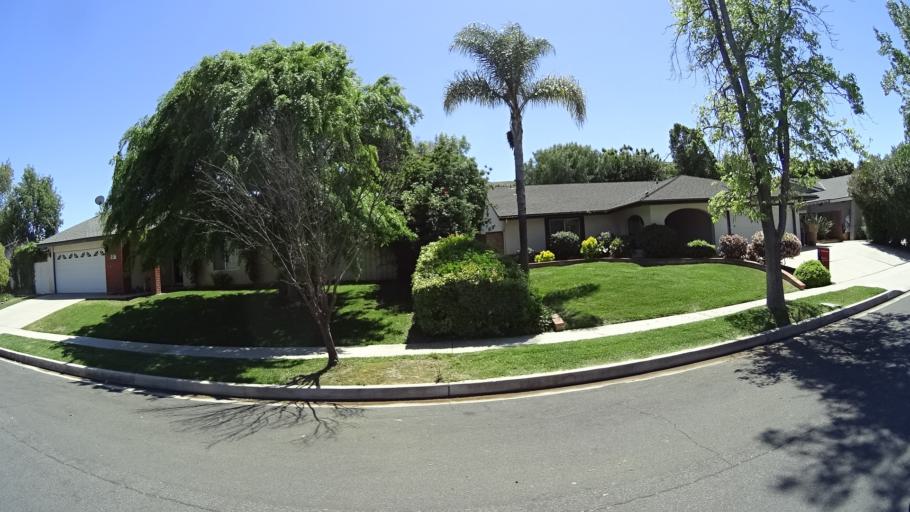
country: US
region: California
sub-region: Ventura County
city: Casa Conejo
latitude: 34.1808
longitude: -118.9006
